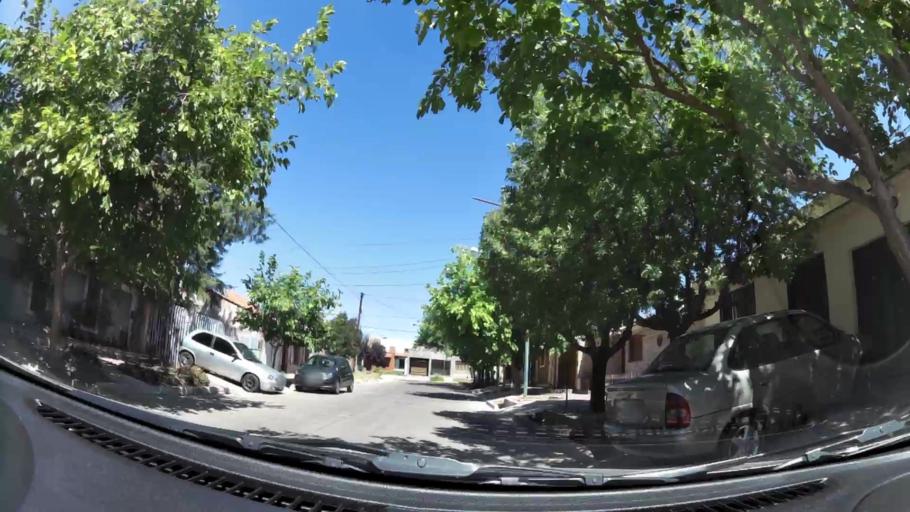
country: AR
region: Mendoza
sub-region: Departamento de Godoy Cruz
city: Godoy Cruz
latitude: -32.9480
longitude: -68.8635
